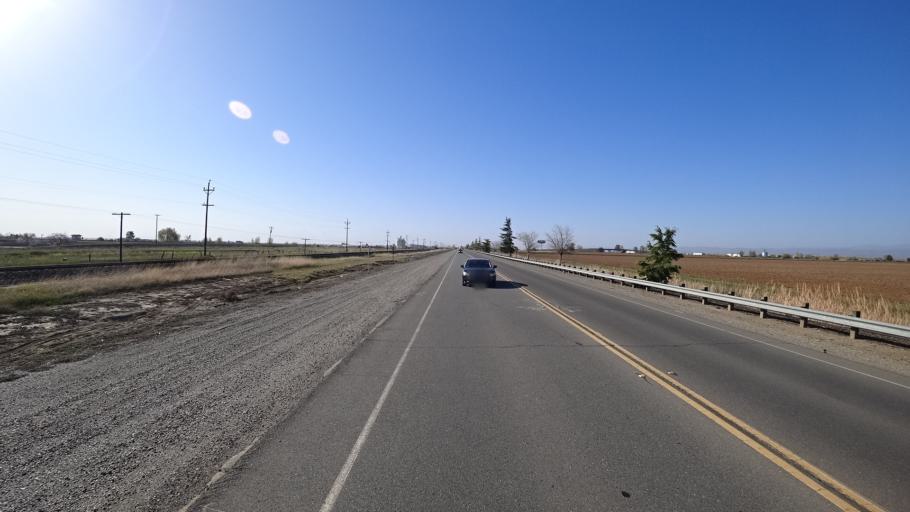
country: US
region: California
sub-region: Glenn County
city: Willows
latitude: 39.5018
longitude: -122.1932
